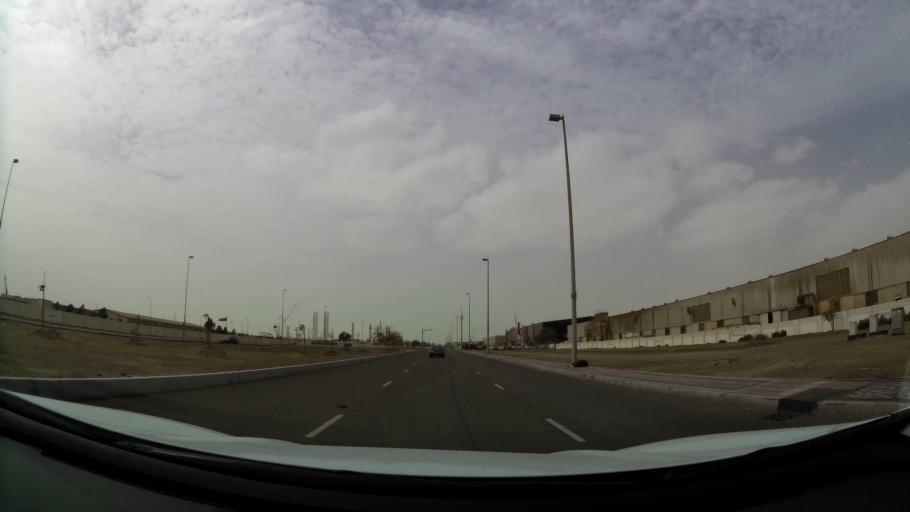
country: AE
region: Abu Dhabi
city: Abu Dhabi
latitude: 24.3675
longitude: 54.4785
